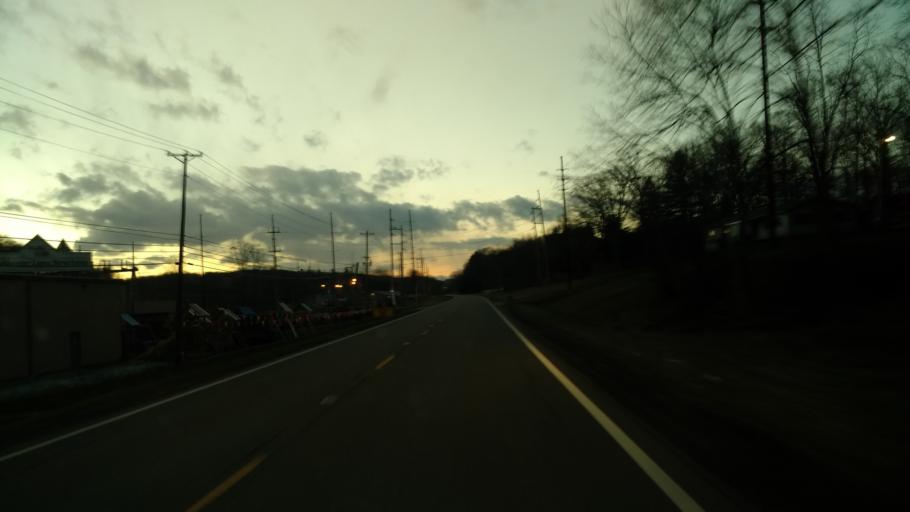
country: US
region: Ohio
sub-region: Holmes County
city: Millersburg
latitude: 40.5608
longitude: -81.9459
